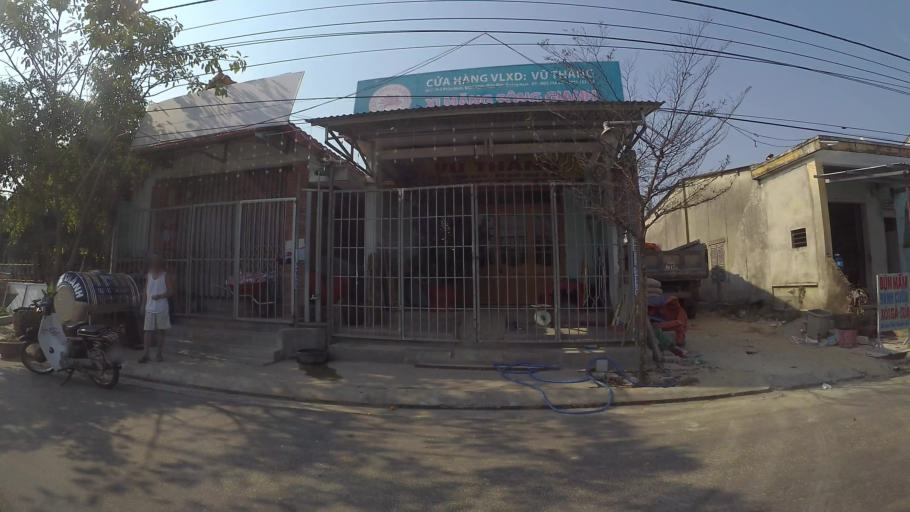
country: VN
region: Da Nang
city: Ngu Hanh Son
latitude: 15.9529
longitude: 108.2767
